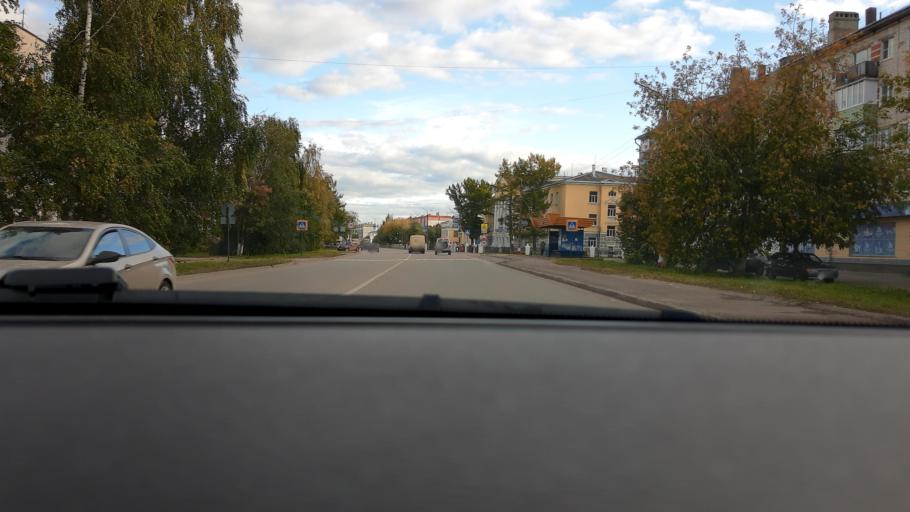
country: RU
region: Nizjnij Novgorod
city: Novaya Balakhna
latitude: 56.5016
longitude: 43.6035
